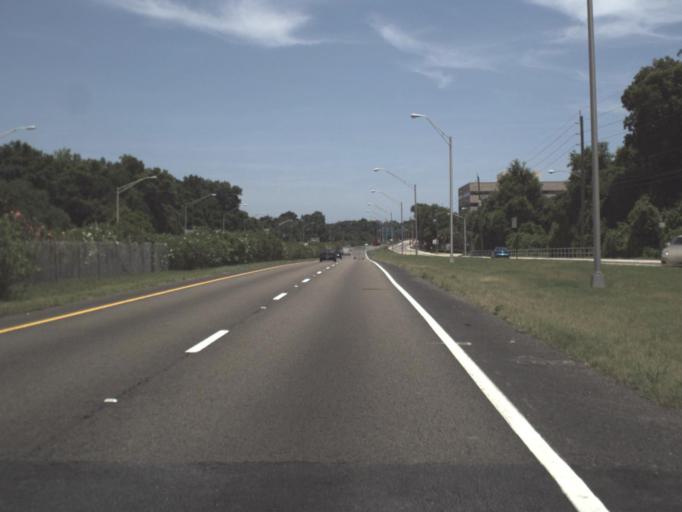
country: US
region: Florida
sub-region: Duval County
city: Jacksonville
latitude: 30.3275
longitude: -81.5779
